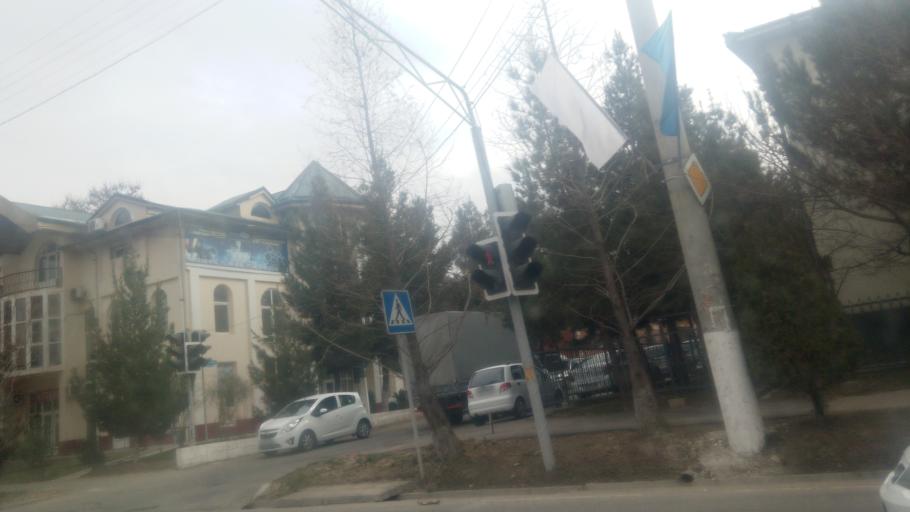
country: UZ
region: Toshkent
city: Salor
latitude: 41.3375
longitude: 69.3294
